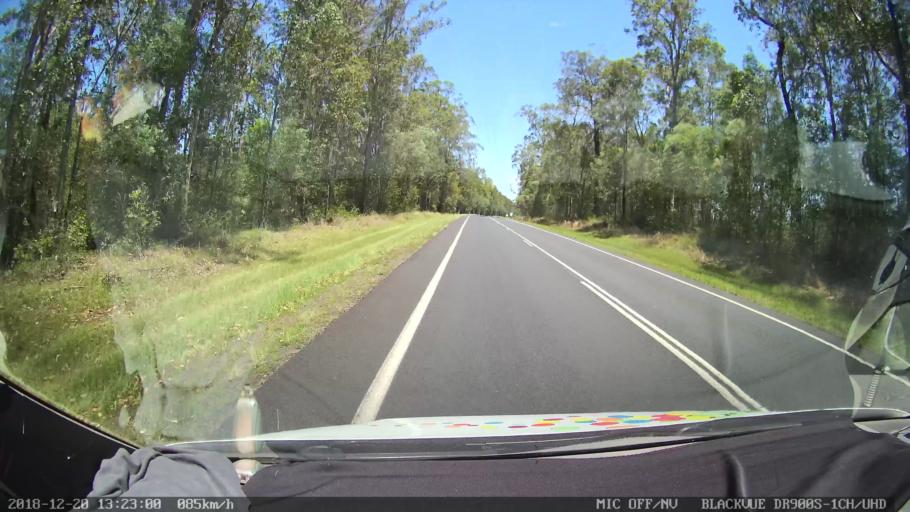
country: AU
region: New South Wales
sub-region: Richmond Valley
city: Casino
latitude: -29.0987
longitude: 153.0010
